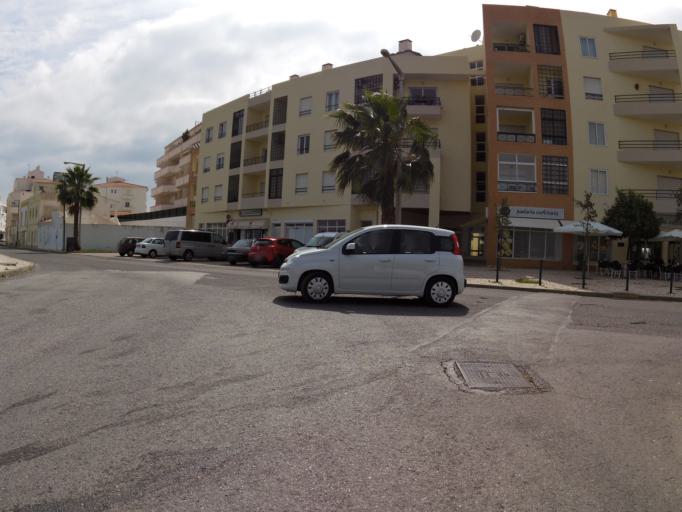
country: PT
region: Faro
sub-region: Silves
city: Armacao de Pera
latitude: 37.1063
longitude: -8.3533
